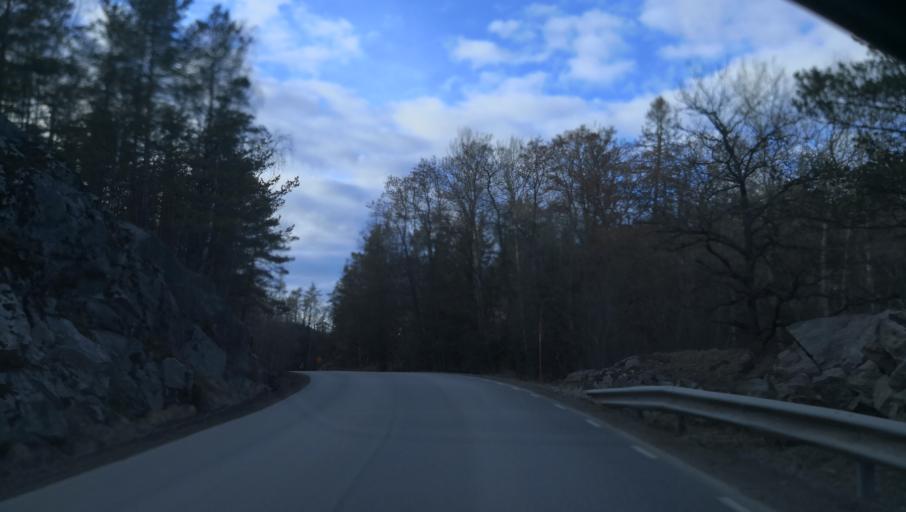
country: SE
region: Stockholm
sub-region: Varmdo Kommun
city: Gustavsberg
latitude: 59.3422
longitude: 18.3571
